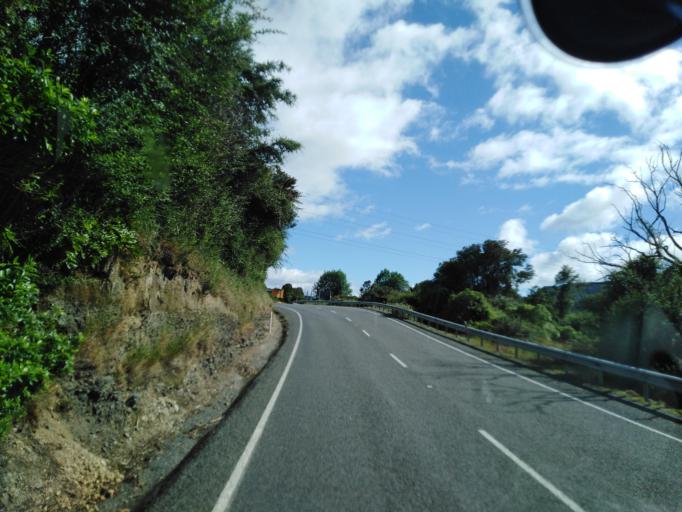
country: NZ
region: Nelson
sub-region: Nelson City
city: Nelson
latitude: -41.2944
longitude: 173.5737
